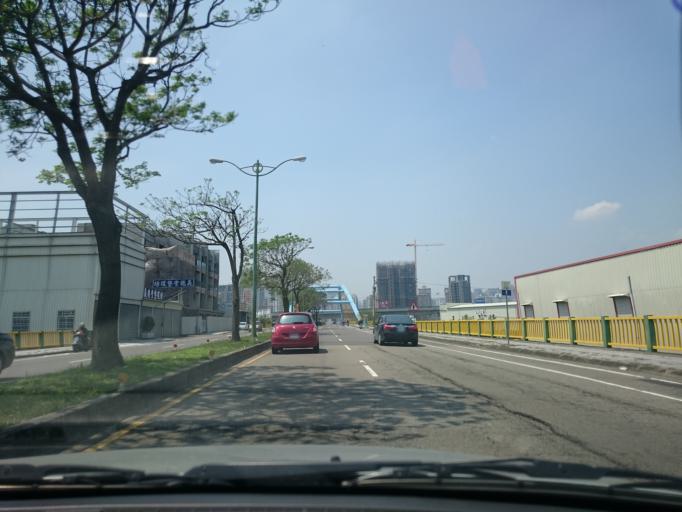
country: TW
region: Taiwan
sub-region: Taichung City
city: Taichung
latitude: 24.1803
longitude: 120.6315
